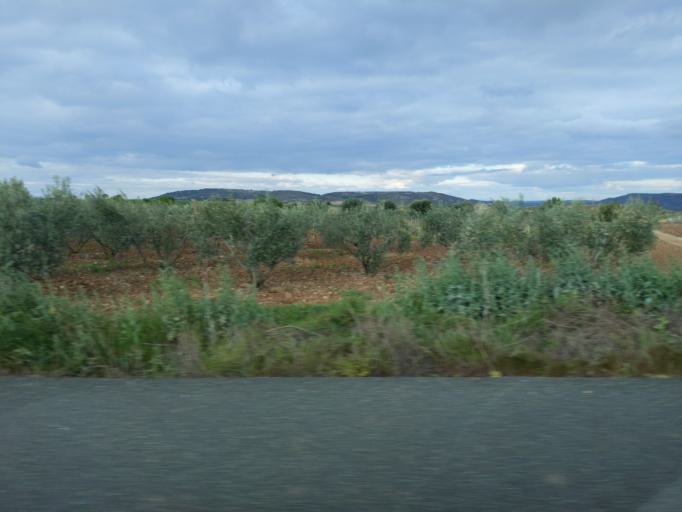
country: ES
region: La Rioja
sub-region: Provincia de La Rioja
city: Corera
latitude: 42.3802
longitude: -2.2061
